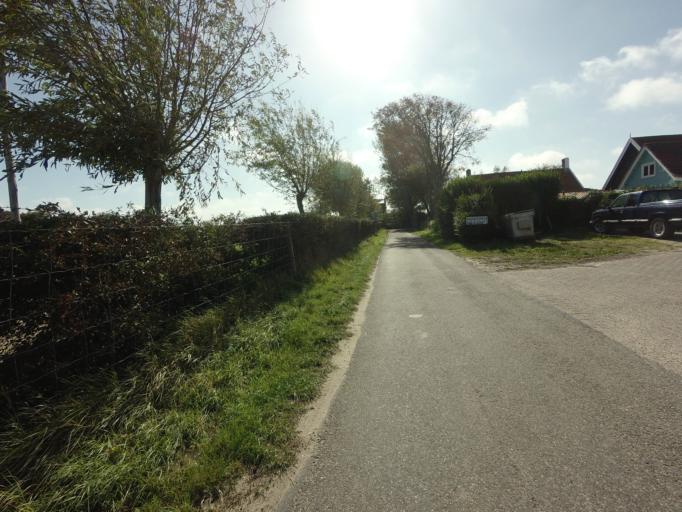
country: NL
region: Zeeland
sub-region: Gemeente Vlissingen
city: Vlissingen
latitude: 51.4792
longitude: 3.5353
